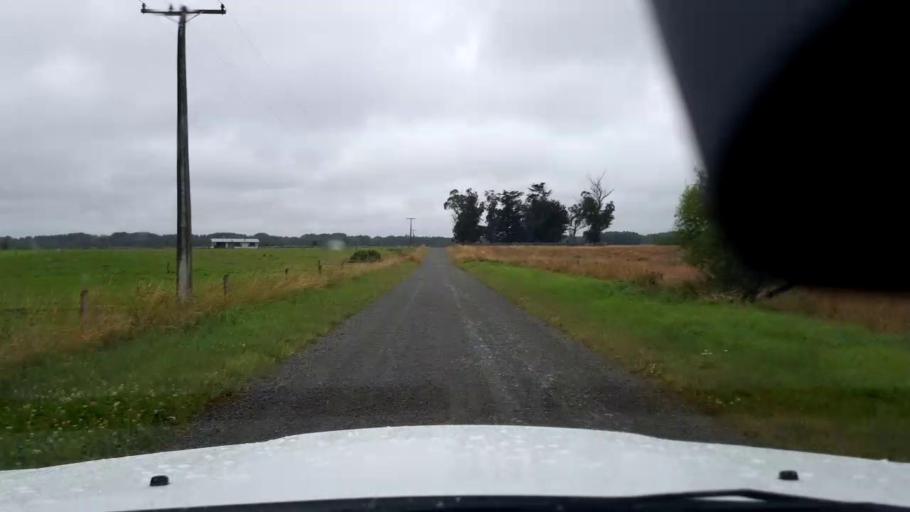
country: NZ
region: Canterbury
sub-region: Timaru District
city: Pleasant Point
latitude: -44.2486
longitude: 171.2007
